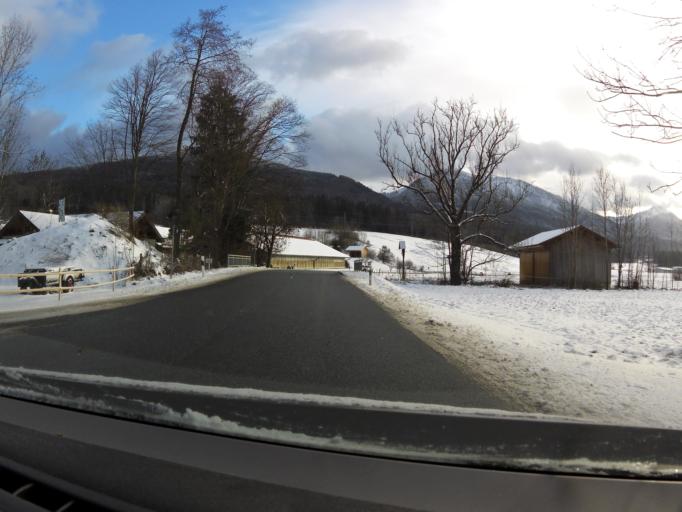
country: DE
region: Bavaria
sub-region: Upper Bavaria
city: Benediktbeuern
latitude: 47.6921
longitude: 11.4063
